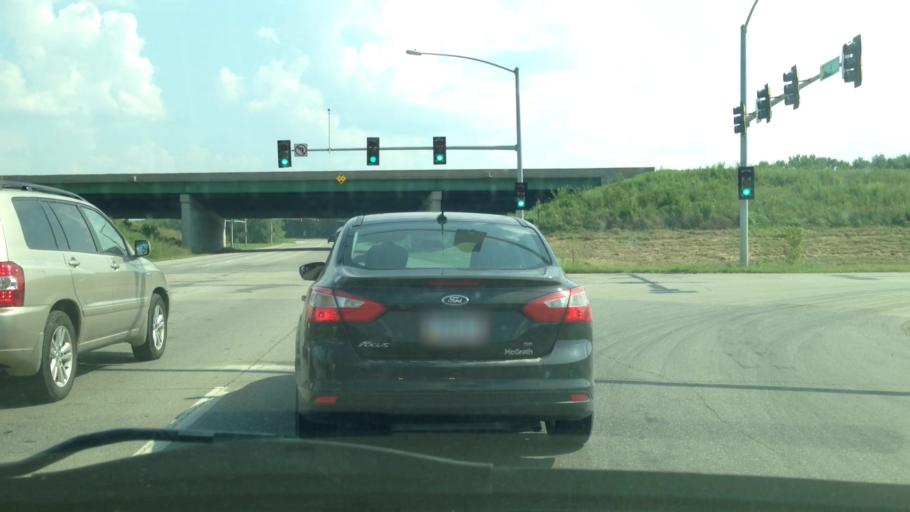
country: US
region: Iowa
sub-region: Black Hawk County
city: Cedar Falls
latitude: 42.5400
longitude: -92.3951
